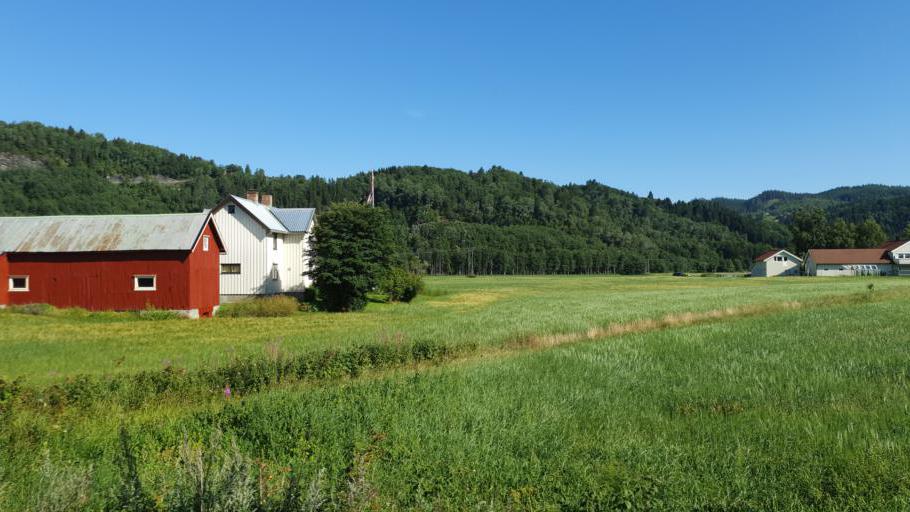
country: NO
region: Sor-Trondelag
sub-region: Orkdal
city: Orkanger
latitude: 63.2059
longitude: 9.7848
